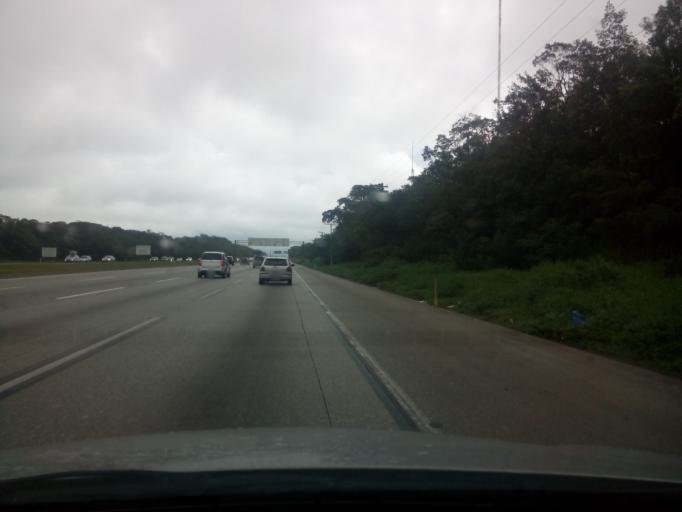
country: BR
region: Sao Paulo
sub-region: Cubatao
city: Cubatao
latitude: -23.9158
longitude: -46.5561
